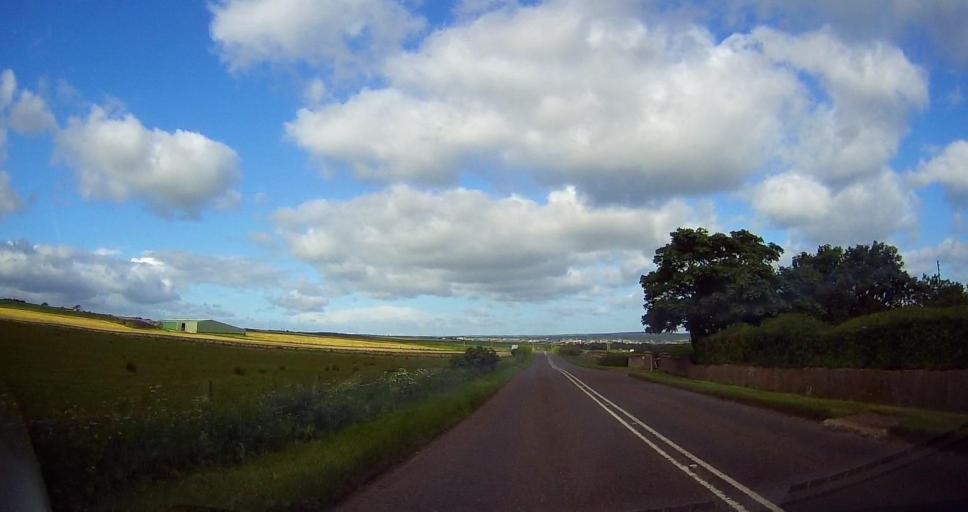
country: GB
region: Scotland
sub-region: Highland
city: Thurso
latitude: 58.5926
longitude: -3.4754
